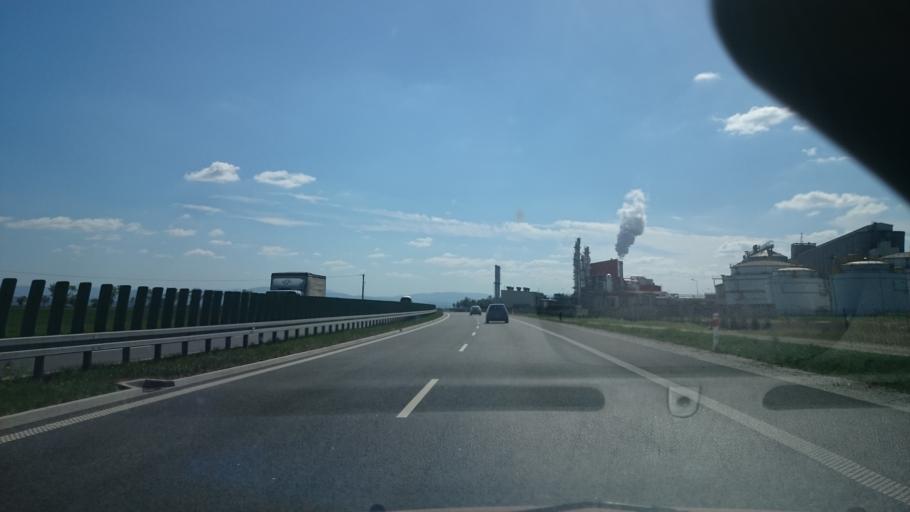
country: PL
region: Opole Voivodeship
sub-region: Powiat nyski
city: Nysa
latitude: 50.4832
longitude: 17.2677
